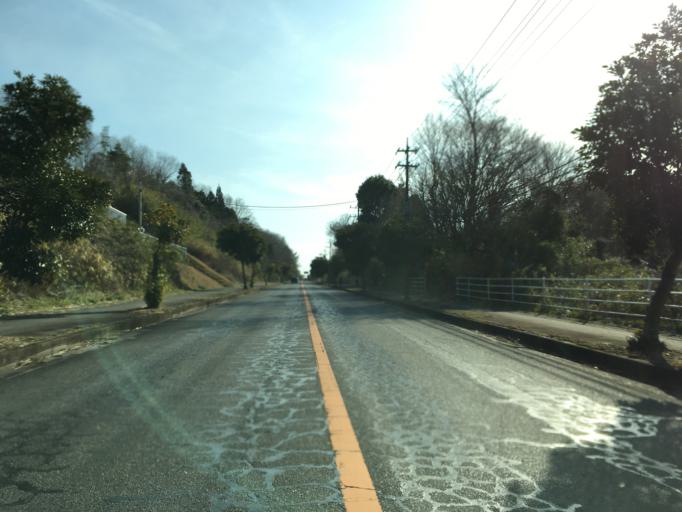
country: JP
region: Ibaraki
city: Takahagi
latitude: 36.7586
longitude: 140.7096
